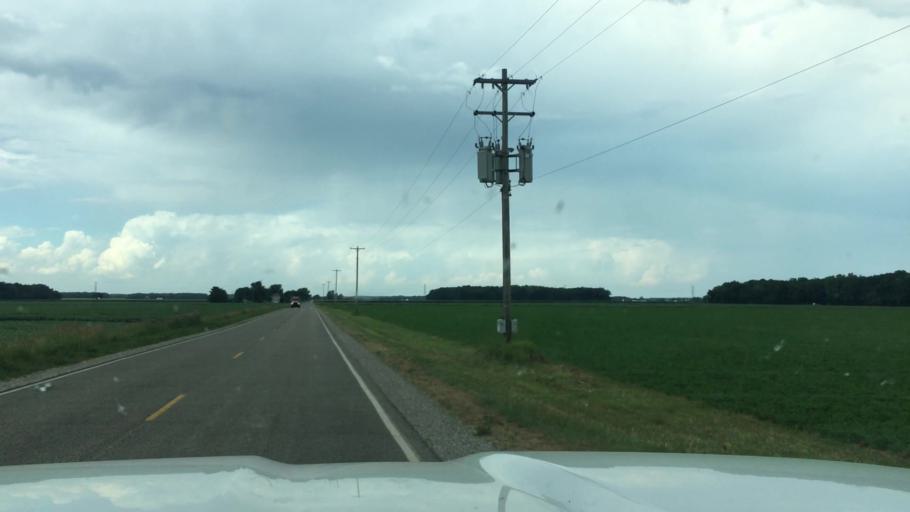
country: US
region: Michigan
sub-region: Montcalm County
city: Carson City
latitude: 43.1938
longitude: -84.7779
